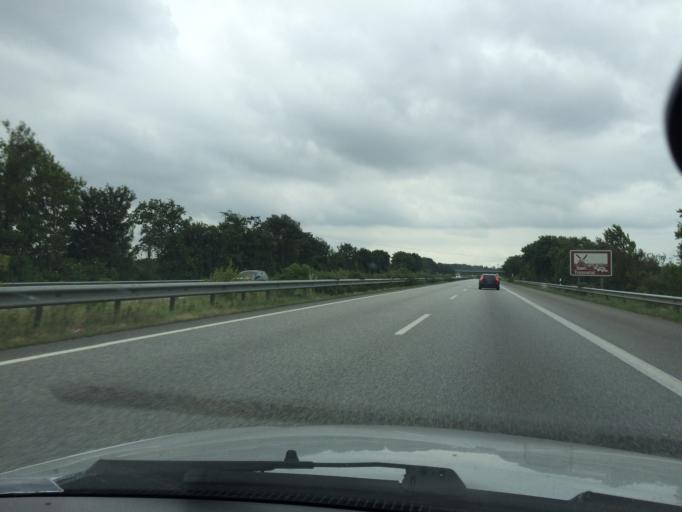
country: DE
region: Schleswig-Holstein
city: Tarp
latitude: 54.6834
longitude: 9.4163
